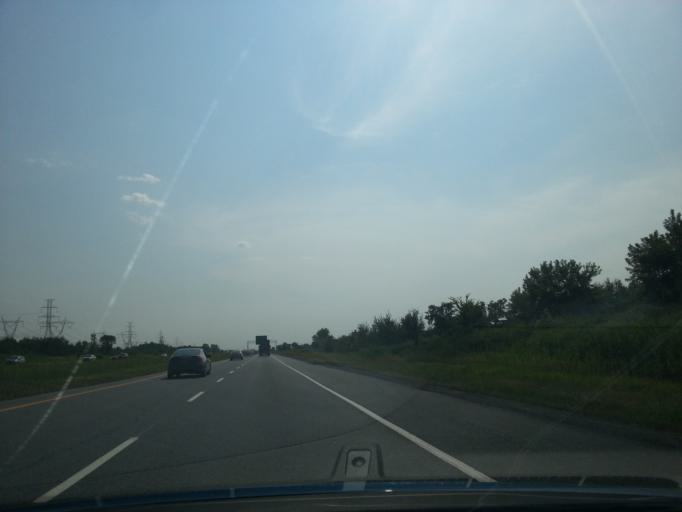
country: CA
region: Quebec
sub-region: Monteregie
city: Brossard
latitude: 45.4658
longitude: -73.3974
